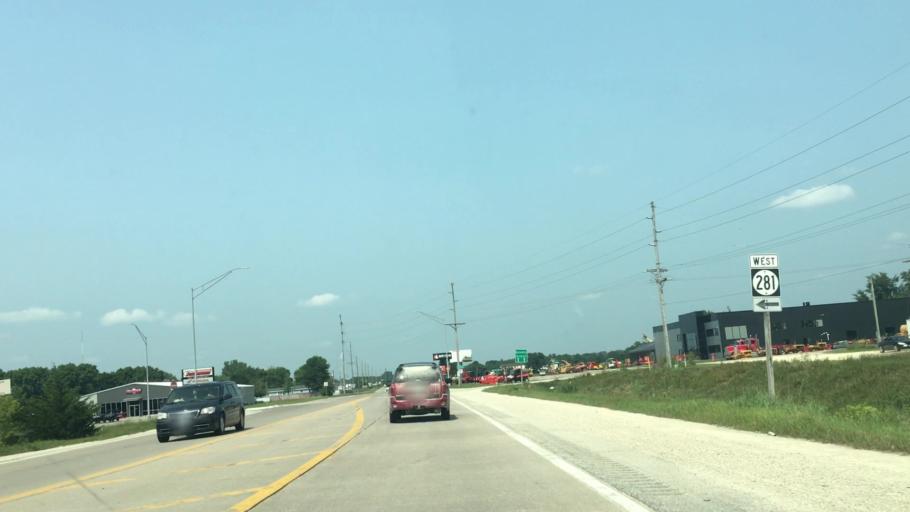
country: US
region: Iowa
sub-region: Fayette County
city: Oelwein
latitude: 42.6413
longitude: -91.9085
